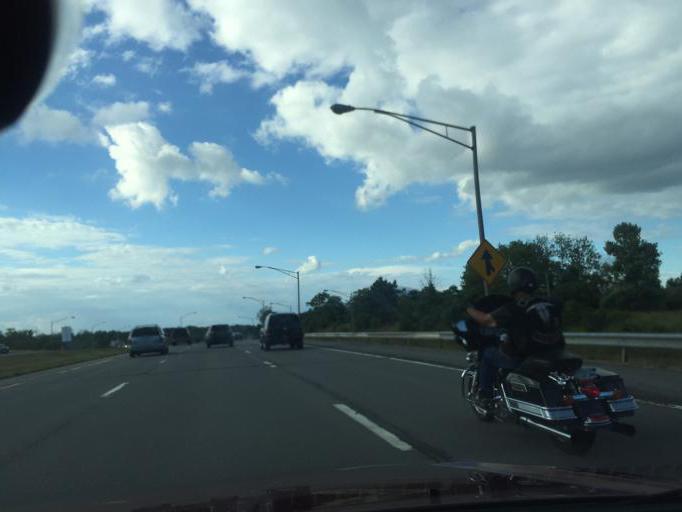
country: US
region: New York
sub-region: Monroe County
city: North Gates
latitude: 43.1793
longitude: -77.6835
